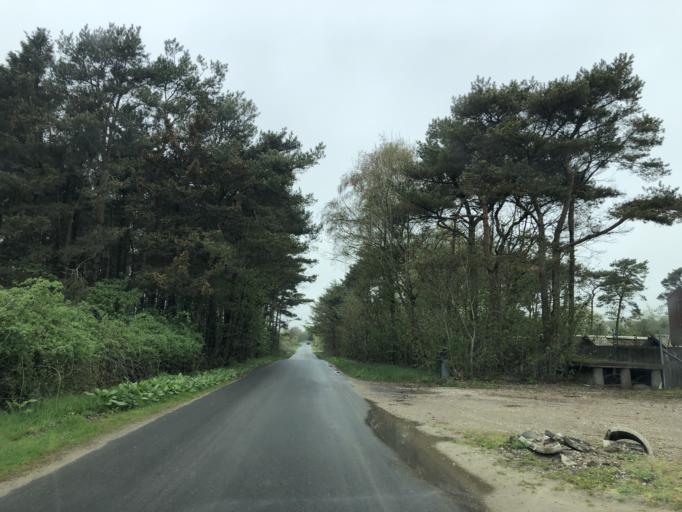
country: DK
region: Central Jutland
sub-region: Lemvig Kommune
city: Lemvig
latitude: 56.5113
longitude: 8.3152
